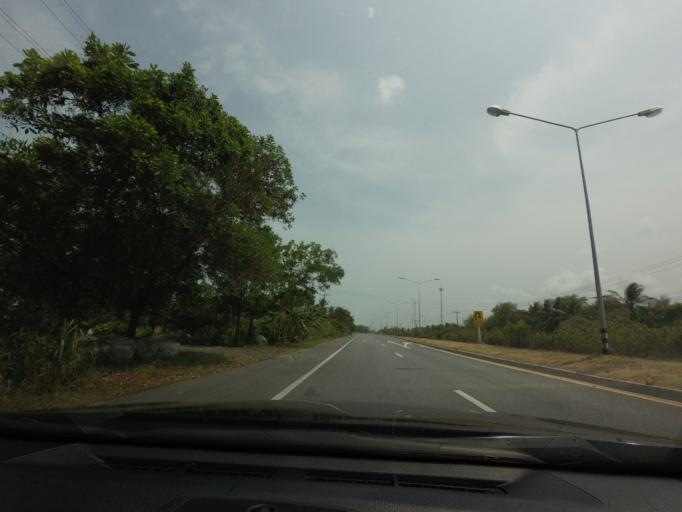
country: TH
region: Nakhon Si Thammarat
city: Hua Sai
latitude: 7.9677
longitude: 100.3283
